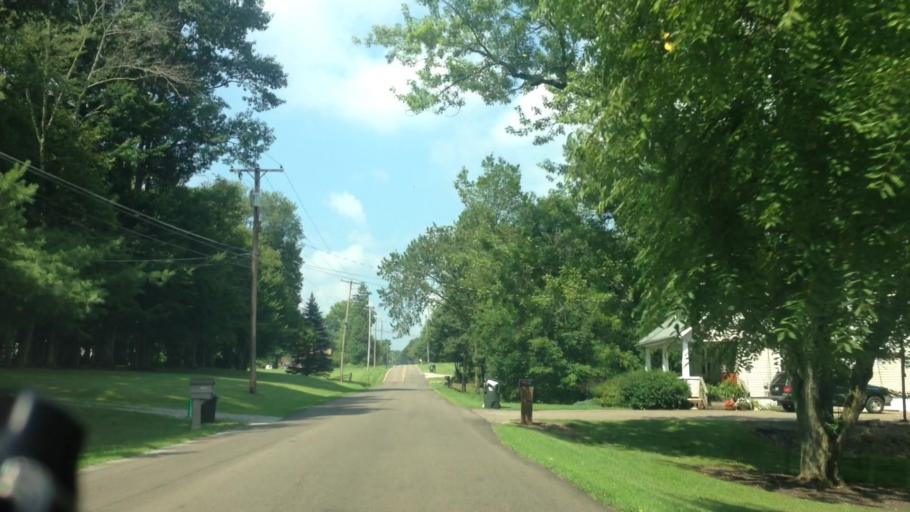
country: US
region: Ohio
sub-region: Stark County
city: Massillon
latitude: 40.8376
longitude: -81.5654
